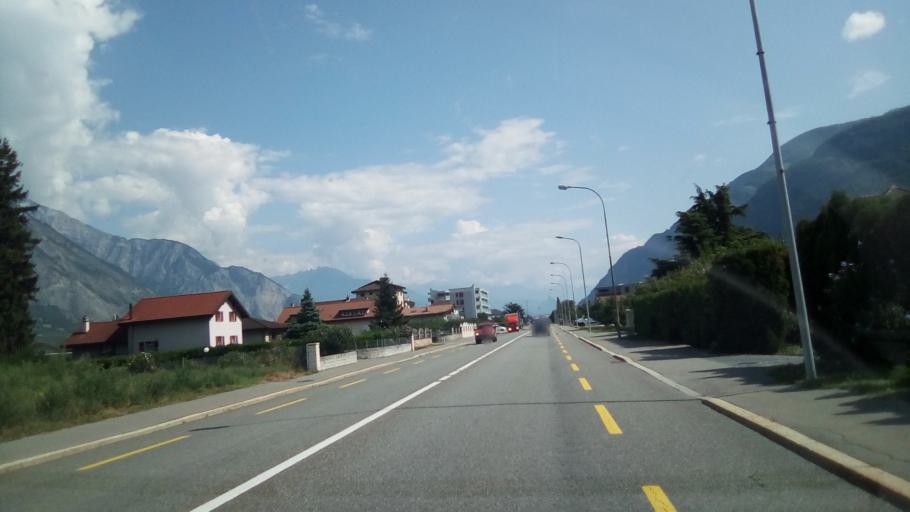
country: CH
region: Valais
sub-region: Martigny District
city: Saxon
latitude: 46.1521
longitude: 7.1808
